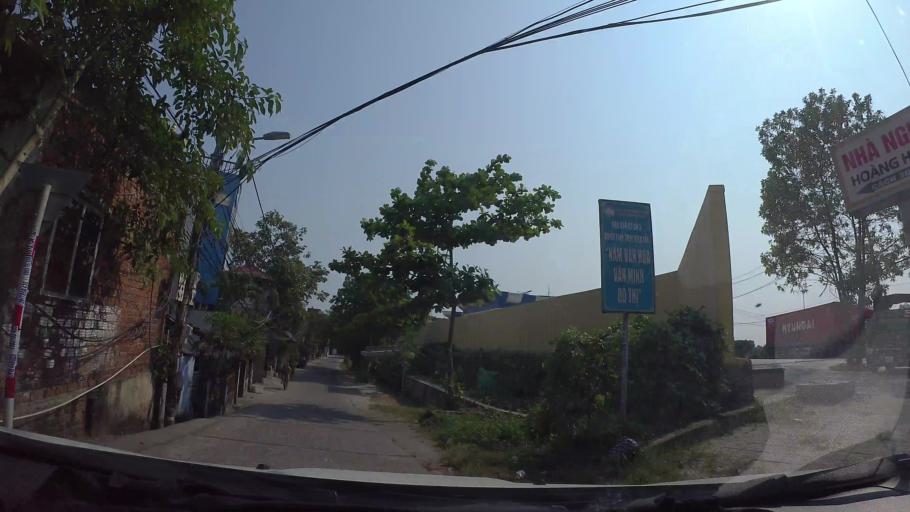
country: VN
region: Da Nang
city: Cam Le
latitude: 16.0101
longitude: 108.1935
